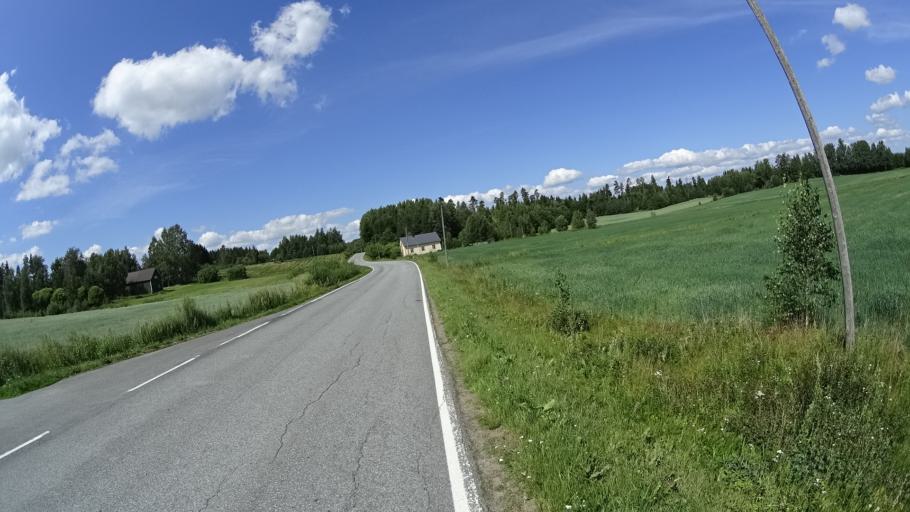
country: FI
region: Haeme
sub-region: Forssa
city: Tammela
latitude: 60.7624
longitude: 23.8813
